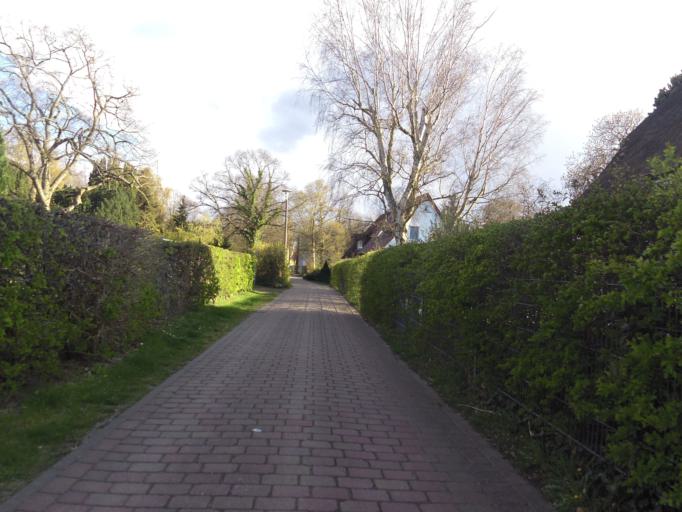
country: DE
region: Mecklenburg-Vorpommern
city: Zingst
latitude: 54.4391
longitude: 12.6883
